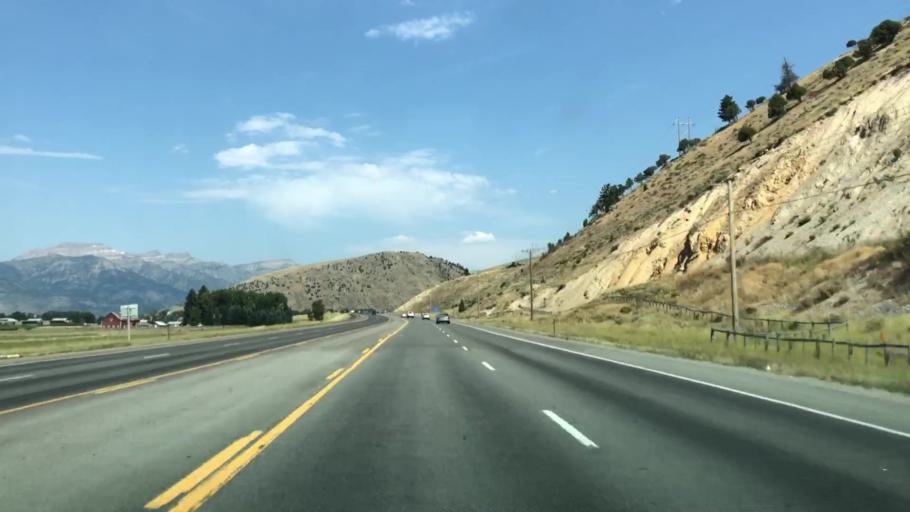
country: US
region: Wyoming
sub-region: Teton County
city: Rafter J Ranch
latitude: 43.4458
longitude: -110.7898
